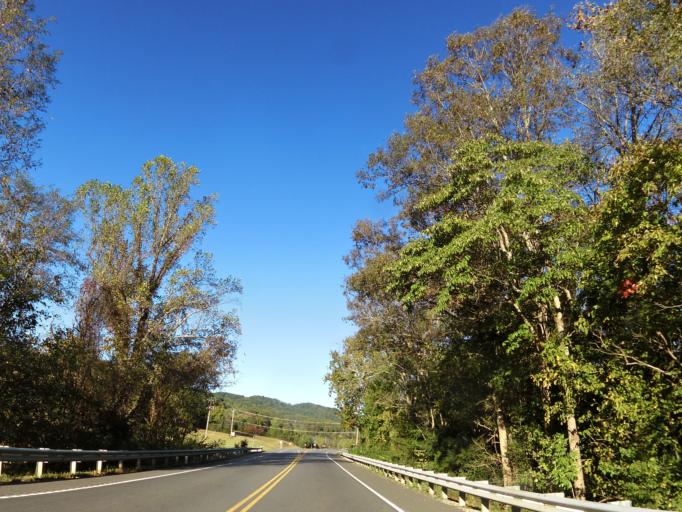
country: US
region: Tennessee
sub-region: Grainger County
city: Bean Station
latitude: 36.3399
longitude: -83.3414
